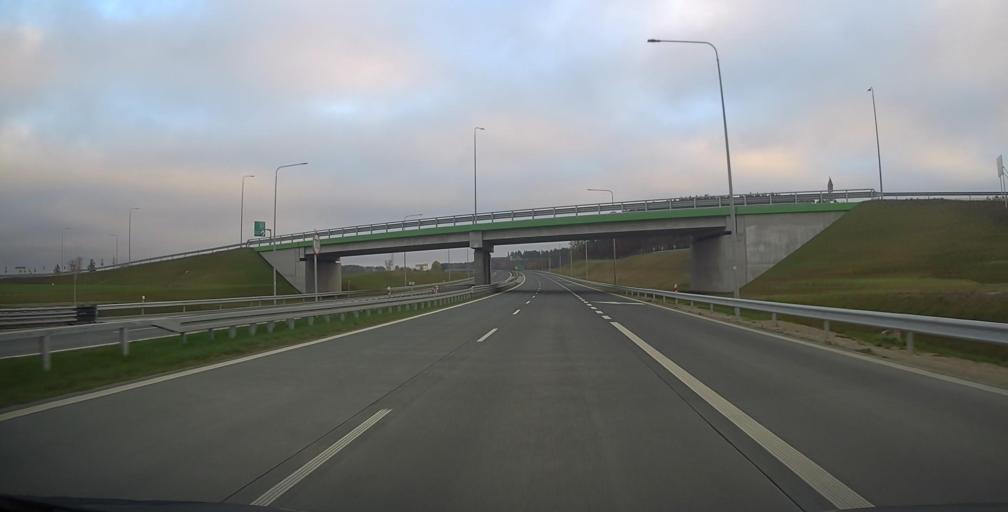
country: PL
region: Podlasie
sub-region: Powiat kolnenski
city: Stawiski
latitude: 53.4575
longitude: 22.1977
